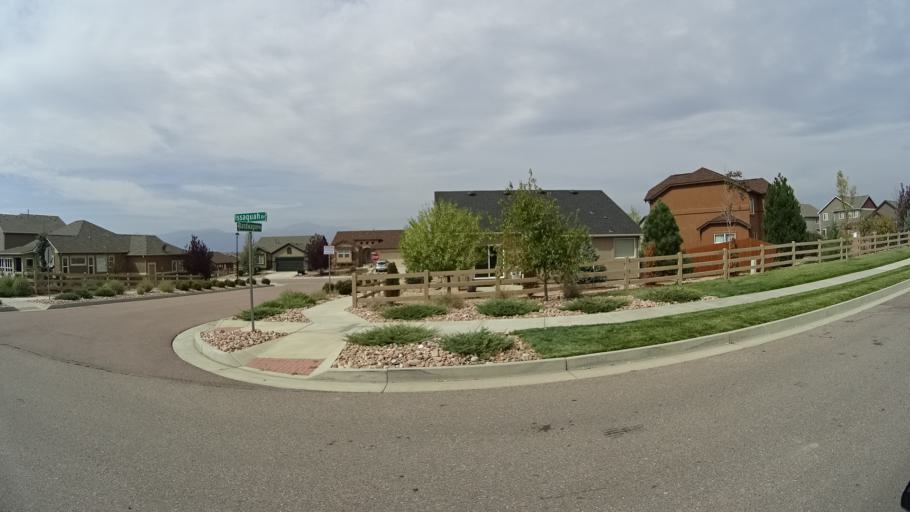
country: US
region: Colorado
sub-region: El Paso County
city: Cimarron Hills
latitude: 38.9243
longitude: -104.6854
